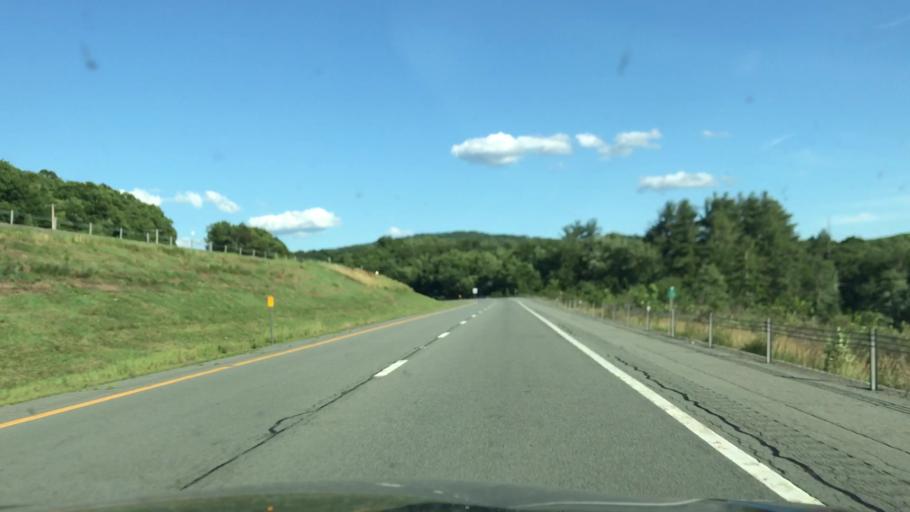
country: US
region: New York
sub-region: Sullivan County
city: Livingston Manor
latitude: 41.9533
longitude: -74.9829
